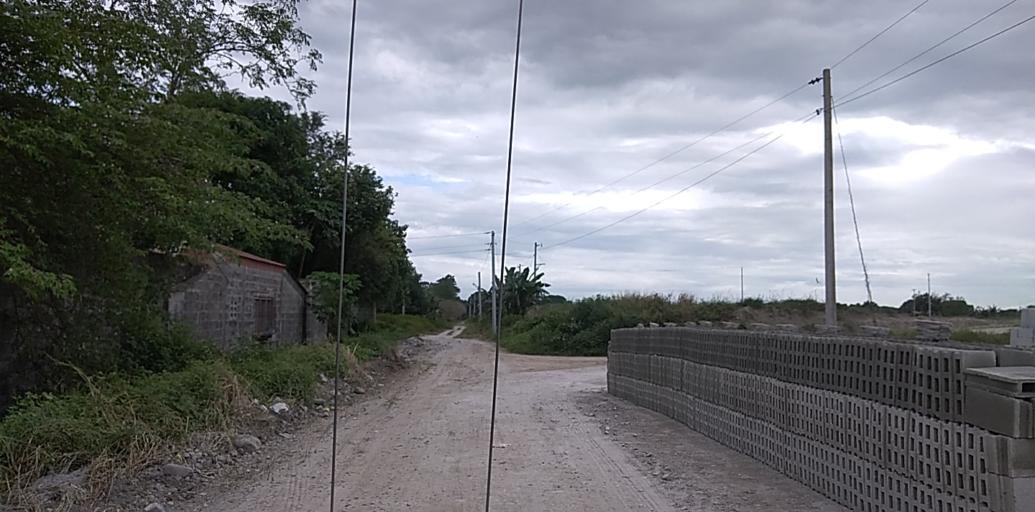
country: PH
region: Central Luzon
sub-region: Province of Pampanga
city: Pulung Santol
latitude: 15.0390
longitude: 120.5591
